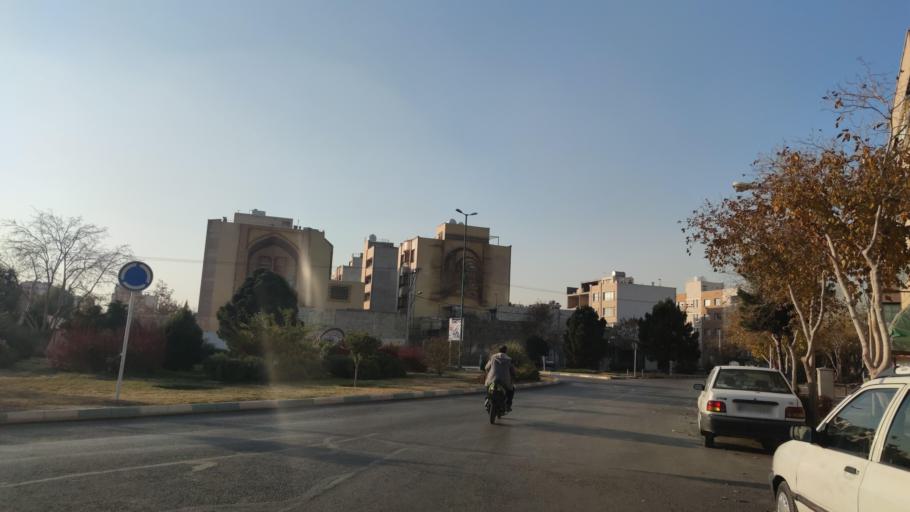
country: IR
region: Isfahan
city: Isfahan
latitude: 32.7078
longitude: 51.6809
